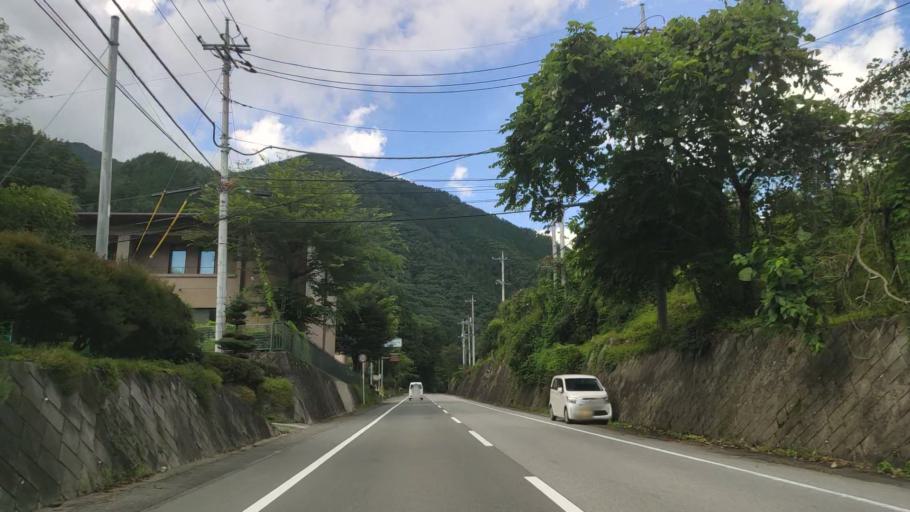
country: JP
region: Yamanashi
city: Enzan
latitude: 35.7926
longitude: 138.7391
